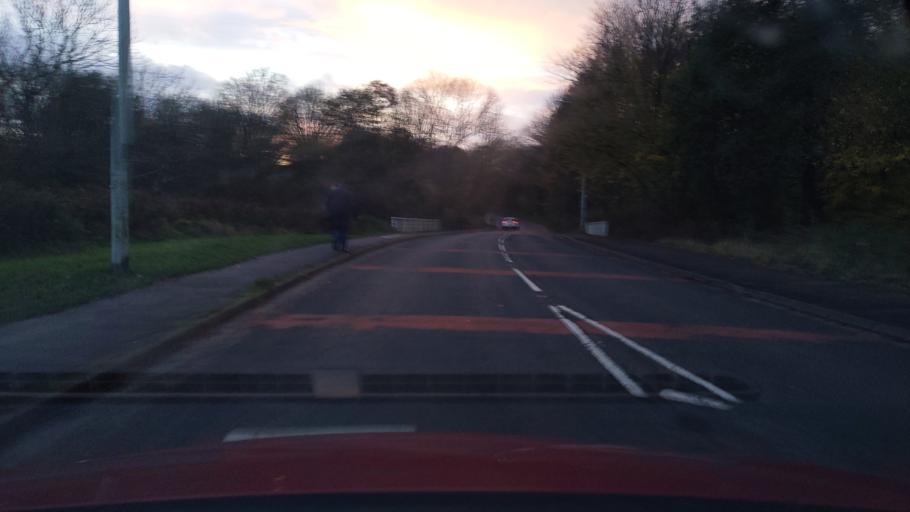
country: GB
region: England
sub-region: Lancashire
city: Clayton-le-Woods
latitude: 53.7002
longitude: -2.6554
